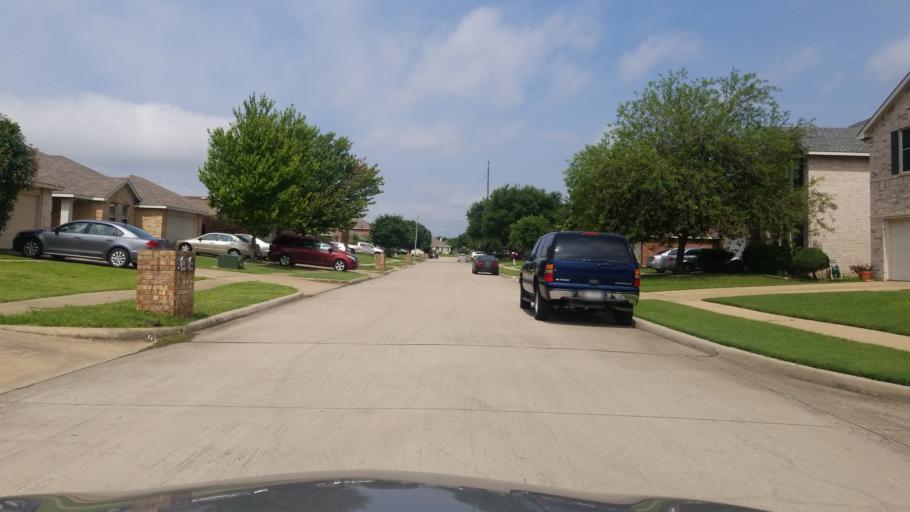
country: US
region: Texas
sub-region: Dallas County
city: Grand Prairie
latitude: 32.6860
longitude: -97.0316
